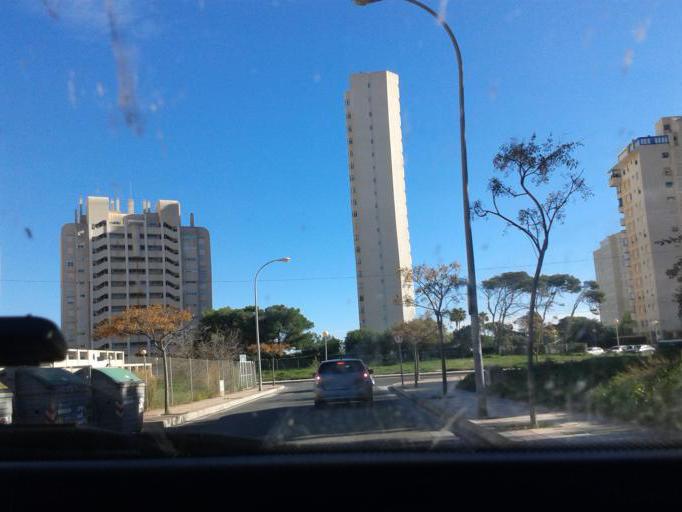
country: ES
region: Valencia
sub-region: Provincia de Alicante
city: el Campello
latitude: 38.4033
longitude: -0.4078
